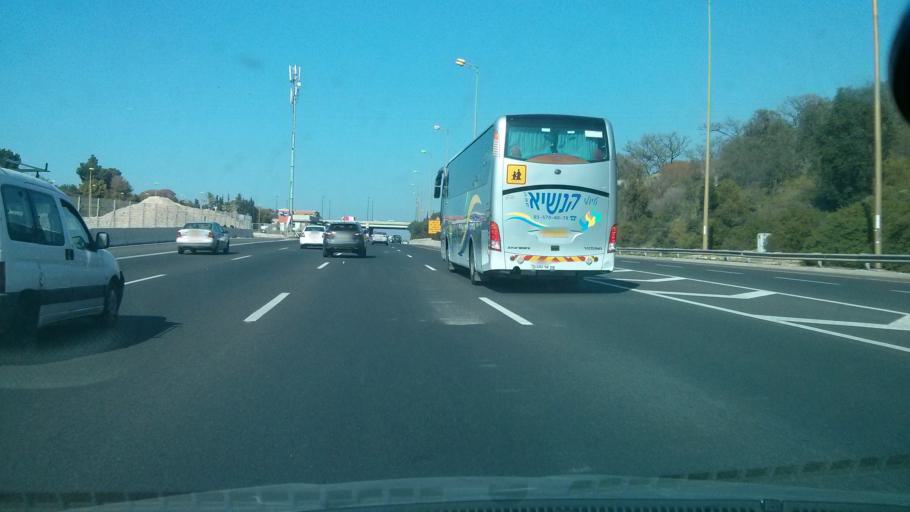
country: IL
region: Tel Aviv
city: Ramat Gan
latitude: 32.1153
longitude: 34.8111
